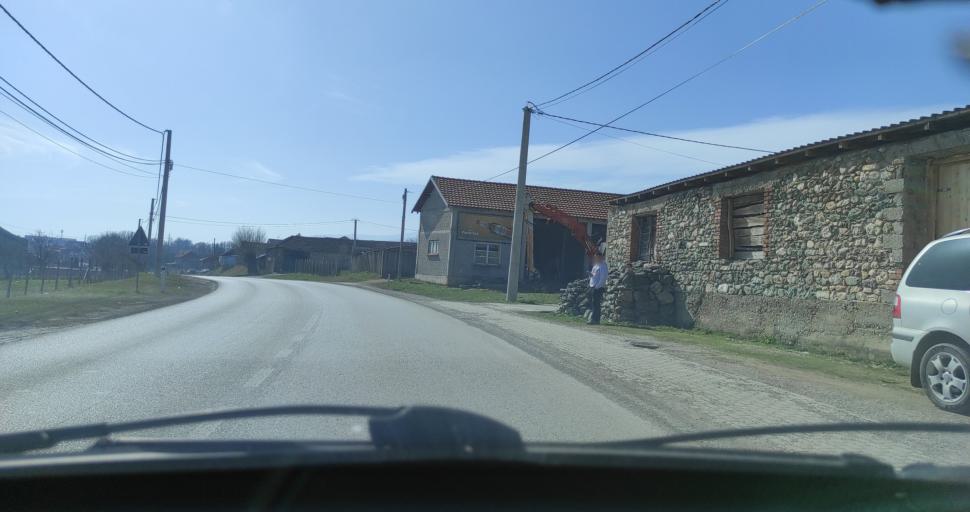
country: XK
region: Gjakova
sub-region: Komuna e Decanit
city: Lebushe
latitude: 42.5612
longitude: 20.2899
